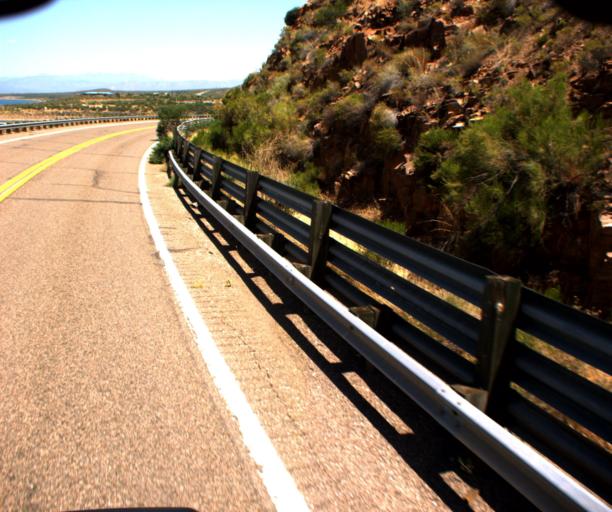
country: US
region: Arizona
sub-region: Gila County
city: Tonto Basin
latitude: 33.6744
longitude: -111.1456
